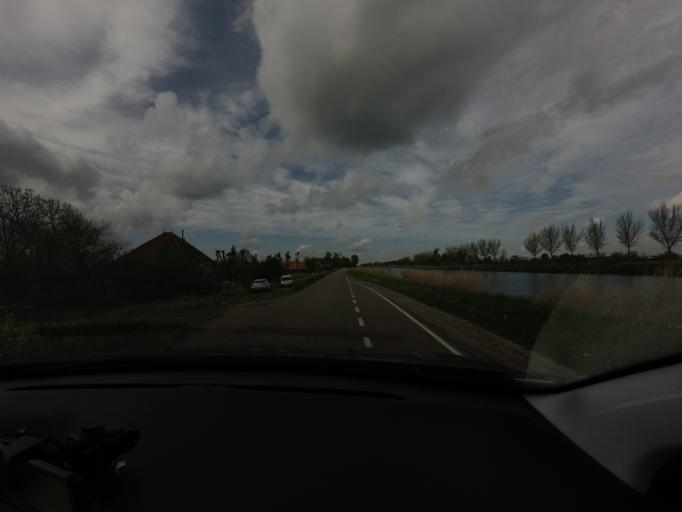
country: NL
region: North Holland
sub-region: Gemeente Beemster
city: Halfweg
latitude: 52.5175
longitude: 4.8918
